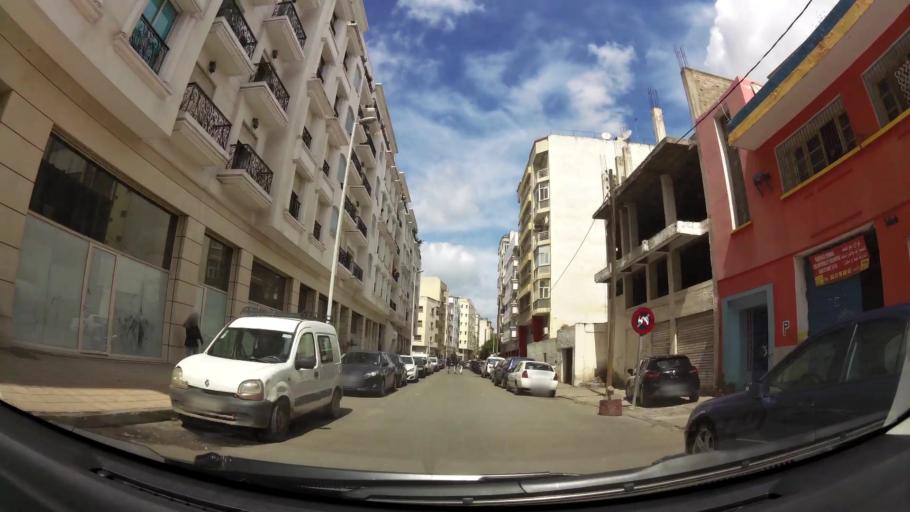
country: MA
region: Grand Casablanca
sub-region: Casablanca
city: Casablanca
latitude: 33.5794
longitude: -7.6376
